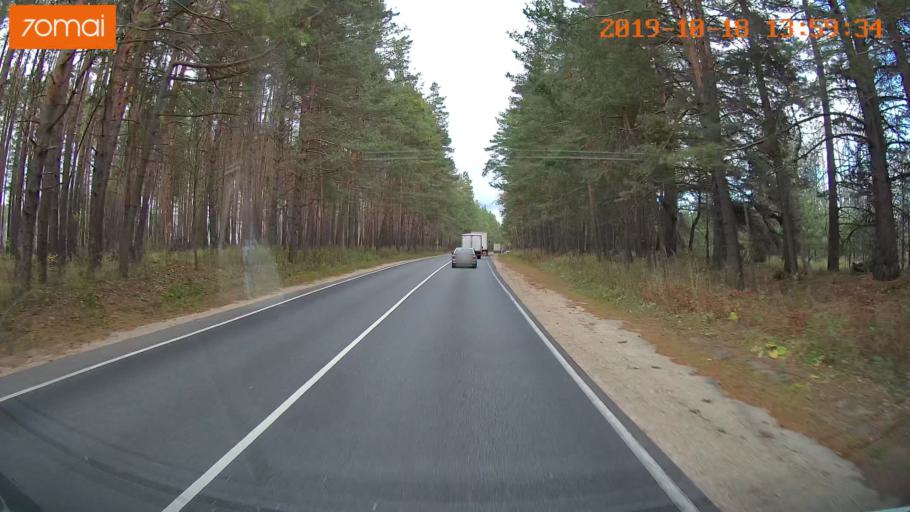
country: RU
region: Rjazan
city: Spas-Klepiki
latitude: 55.0954
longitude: 40.0648
